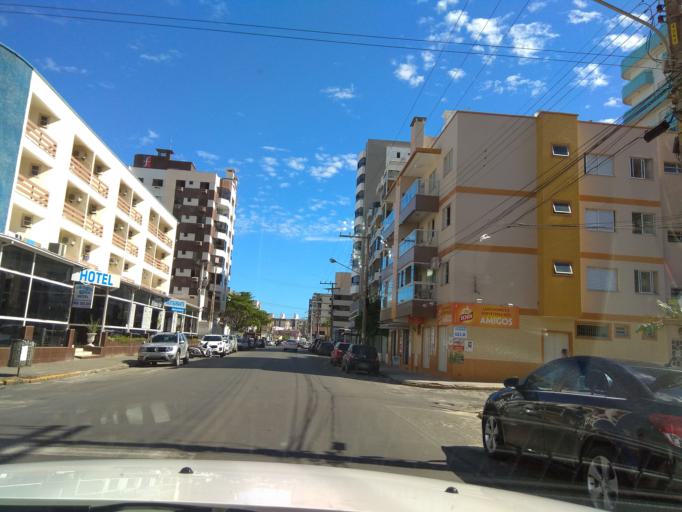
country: BR
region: Santa Catarina
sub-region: Laguna
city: Laguna
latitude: -28.4816
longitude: -48.7690
